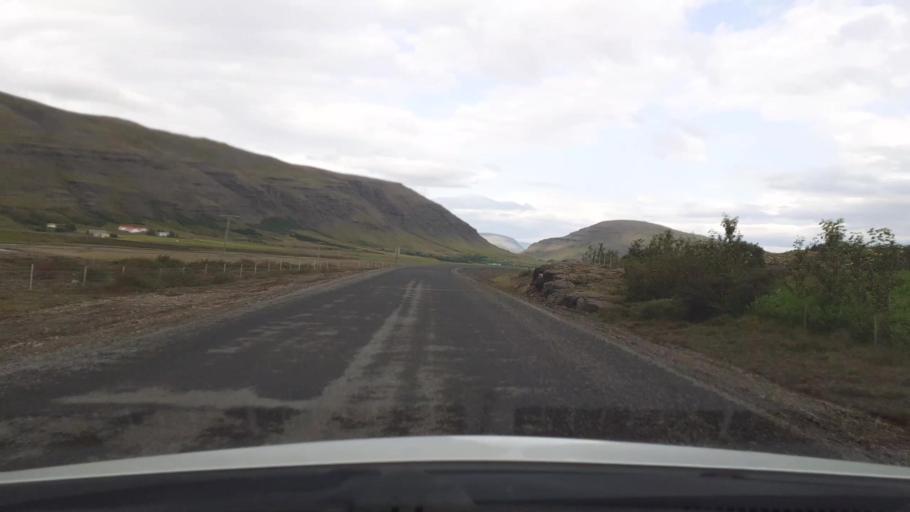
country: IS
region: Capital Region
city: Mosfellsbaer
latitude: 64.2966
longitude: -21.4615
